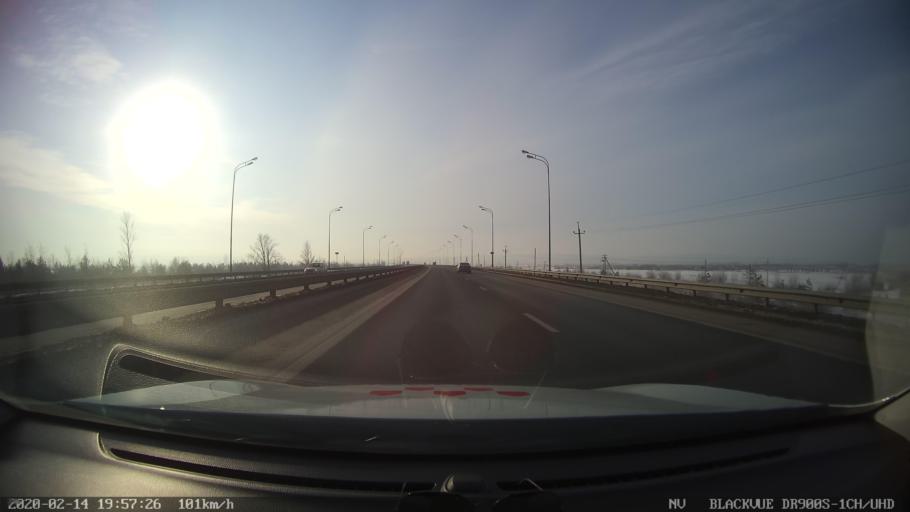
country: RU
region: Tatarstan
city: Osinovo
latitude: 55.8172
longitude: 48.8432
